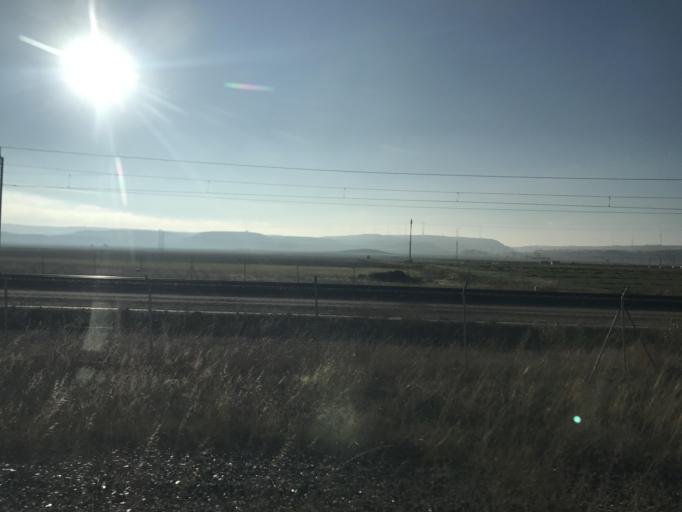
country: ES
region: Castille and Leon
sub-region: Provincia de Palencia
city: Quintana del Puente
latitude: 42.0683
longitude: -4.2168
